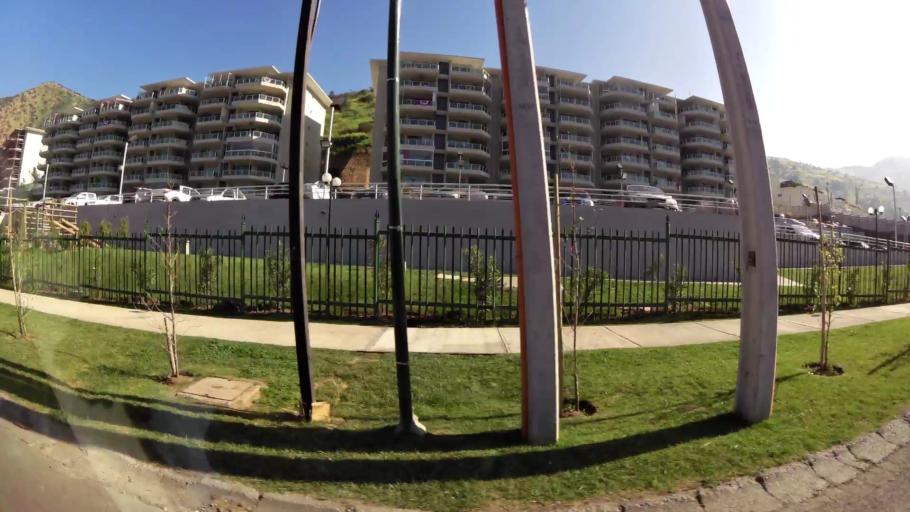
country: CL
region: Santiago Metropolitan
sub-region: Provincia de Chacabuco
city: Chicureo Abajo
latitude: -33.3393
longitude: -70.6692
